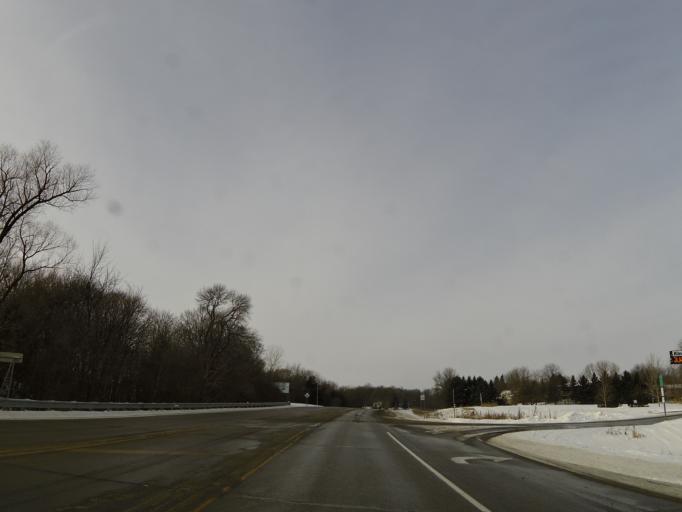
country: US
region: Minnesota
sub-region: Hennepin County
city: Saint Bonifacius
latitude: 44.9020
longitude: -93.7496
